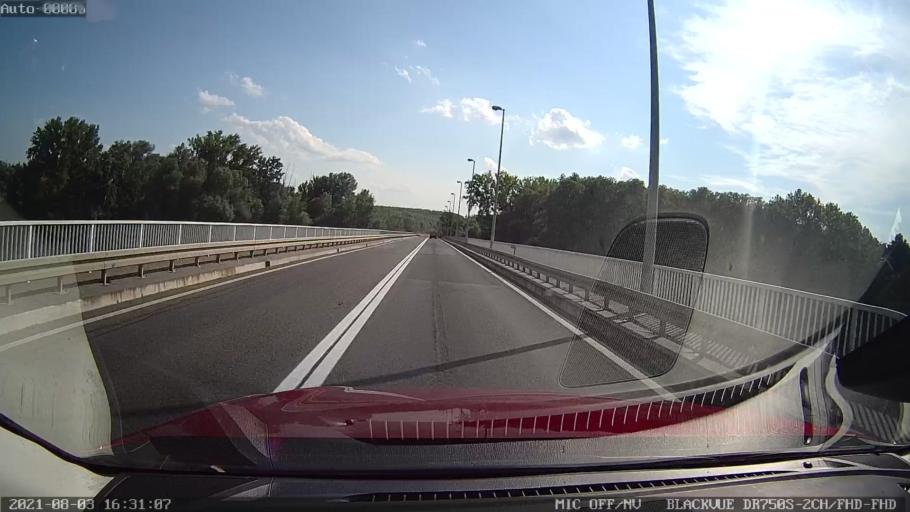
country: HR
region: Osjecko-Baranjska
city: Visnjevac
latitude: 45.5758
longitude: 18.6393
